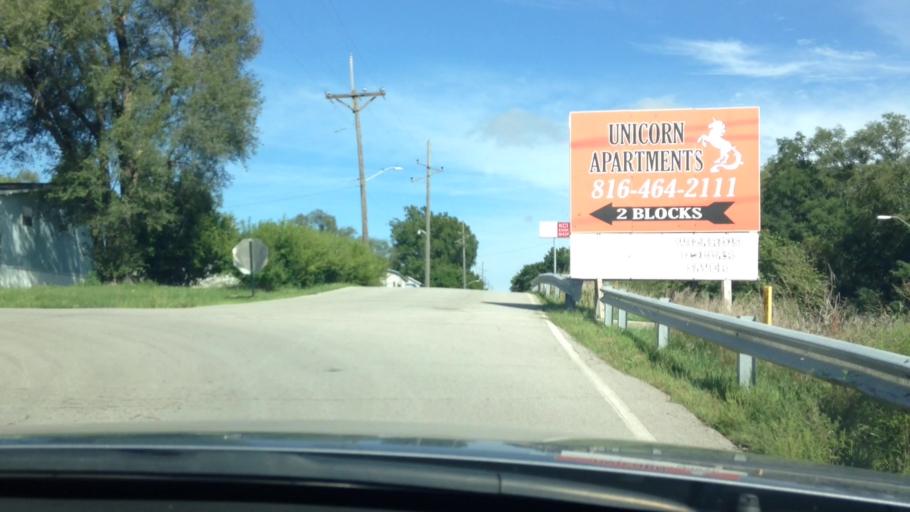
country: US
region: Missouri
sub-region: Platte County
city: Weatherby Lake
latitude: 39.3110
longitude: -94.6668
